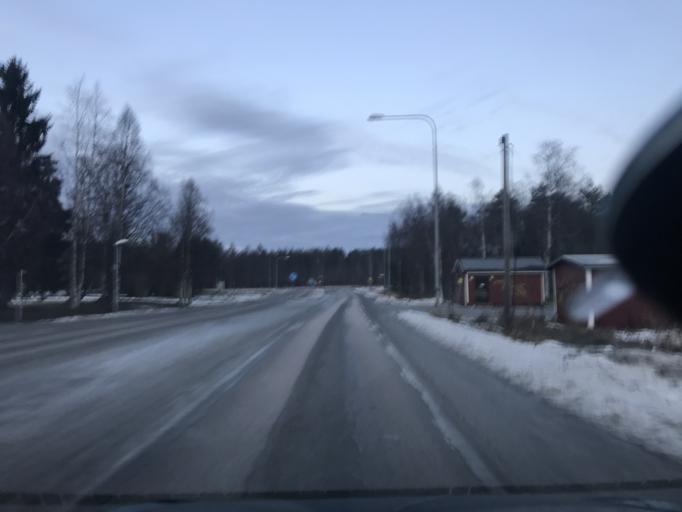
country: SE
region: Norrbotten
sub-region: Lulea Kommun
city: Sodra Sunderbyn
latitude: 65.6541
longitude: 21.9666
